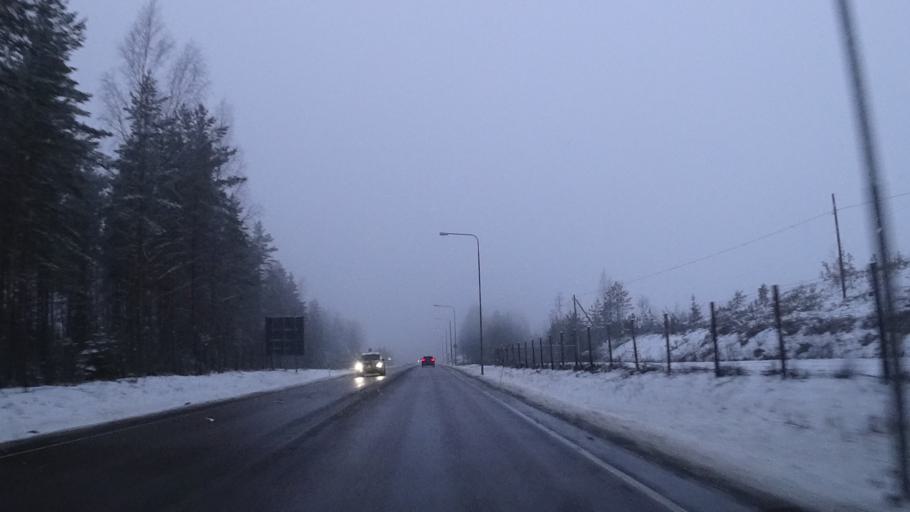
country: FI
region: Paijanne Tavastia
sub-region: Lahti
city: Hollola
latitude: 60.9861
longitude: 25.4042
